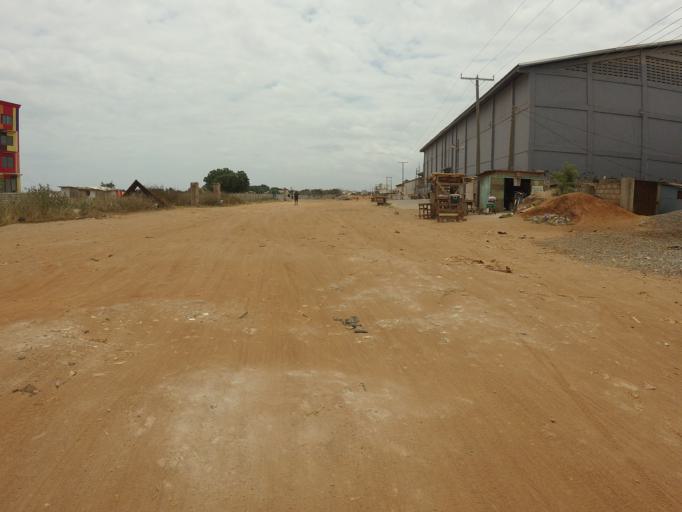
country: GH
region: Greater Accra
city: Medina Estates
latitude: 5.6357
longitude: -0.1269
